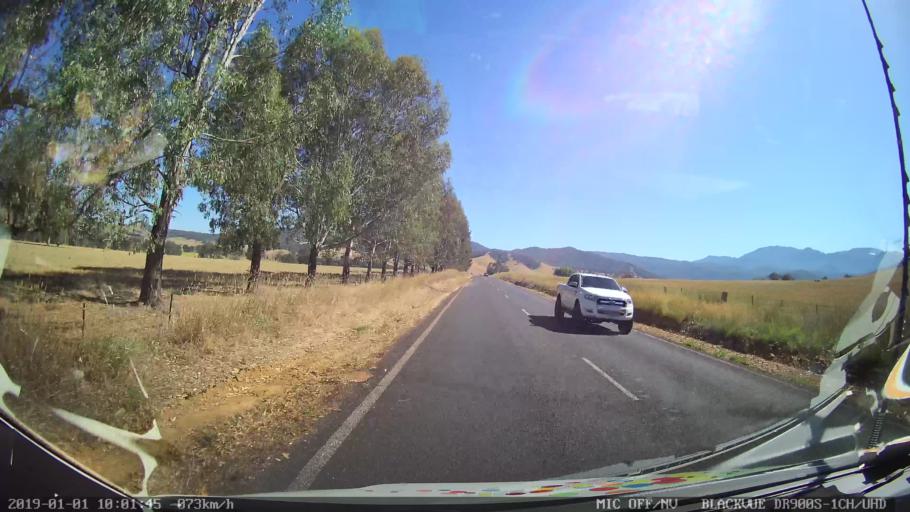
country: AU
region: New South Wales
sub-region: Snowy River
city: Jindabyne
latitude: -36.1883
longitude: 148.1007
